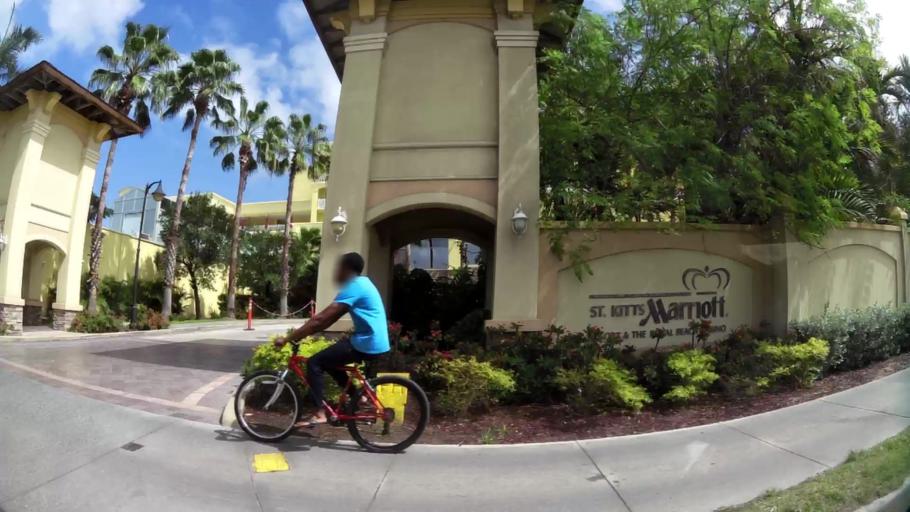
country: KN
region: Saint Peter Basseterre
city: Monkey Hill
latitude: 17.2927
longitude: -62.6859
